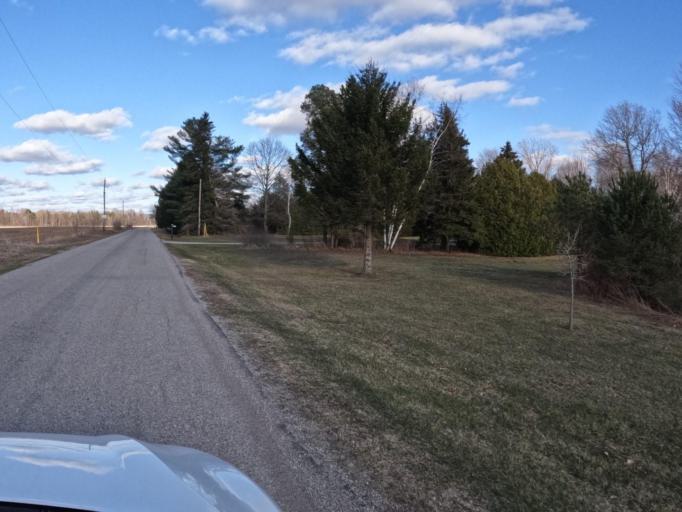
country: CA
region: Ontario
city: Norfolk County
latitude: 42.8152
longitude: -80.5747
